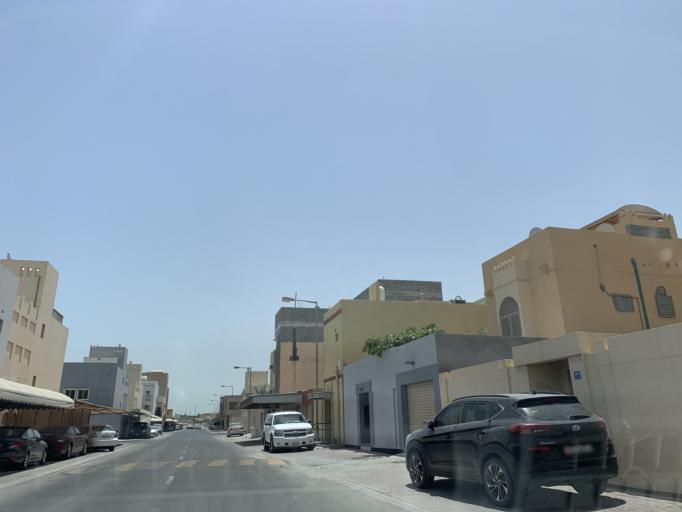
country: BH
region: Northern
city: Sitrah
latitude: 26.1412
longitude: 50.5936
